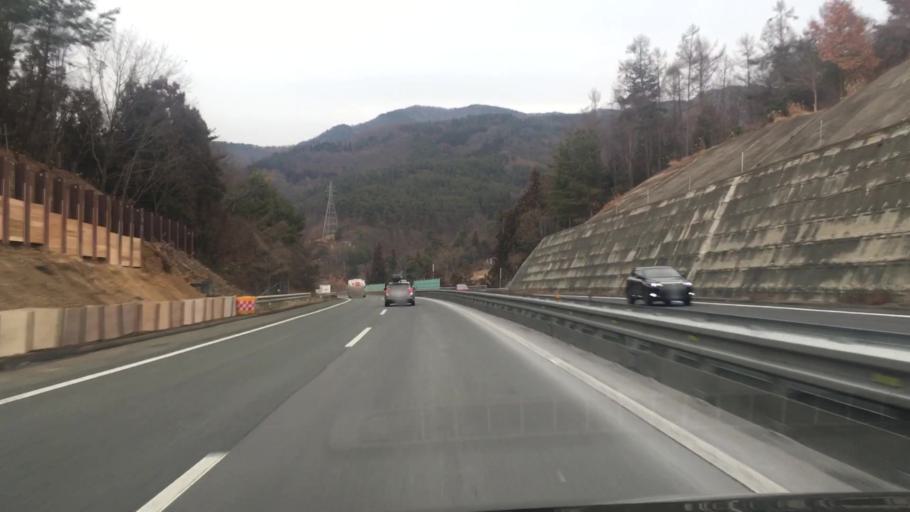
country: JP
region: Nagano
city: Ueda
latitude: 36.4670
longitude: 138.1983
